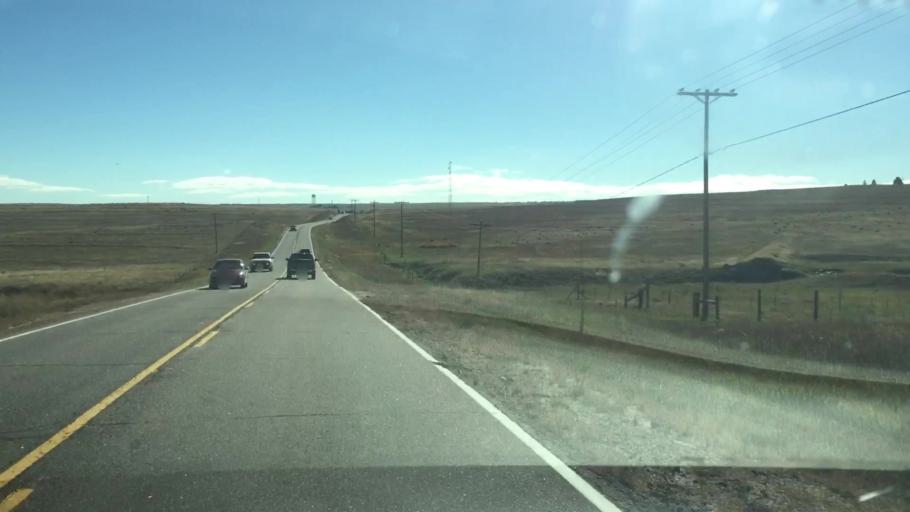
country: US
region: Colorado
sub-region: Elbert County
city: Kiowa
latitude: 39.3508
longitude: -104.4883
